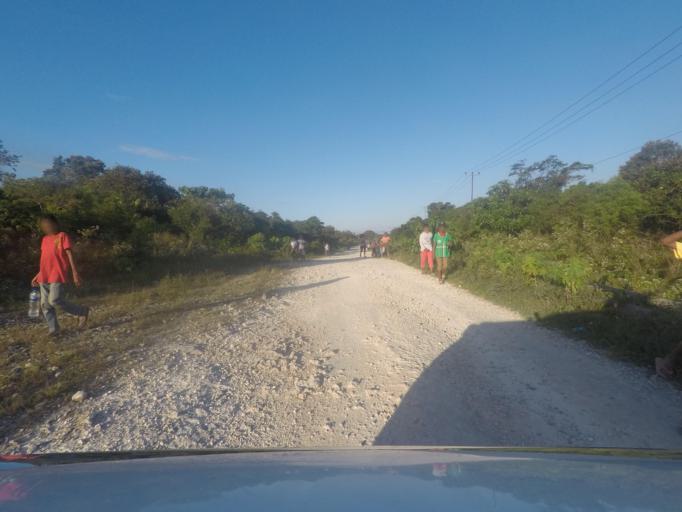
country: TL
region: Lautem
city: Lospalos
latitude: -8.3991
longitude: 127.2027
